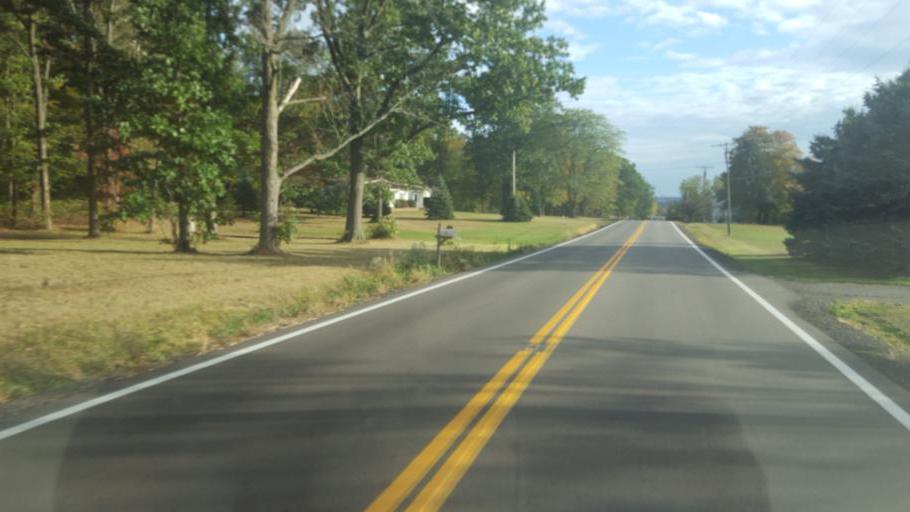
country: US
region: Ohio
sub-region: Ashland County
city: Ashland
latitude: 40.8421
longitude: -82.2128
